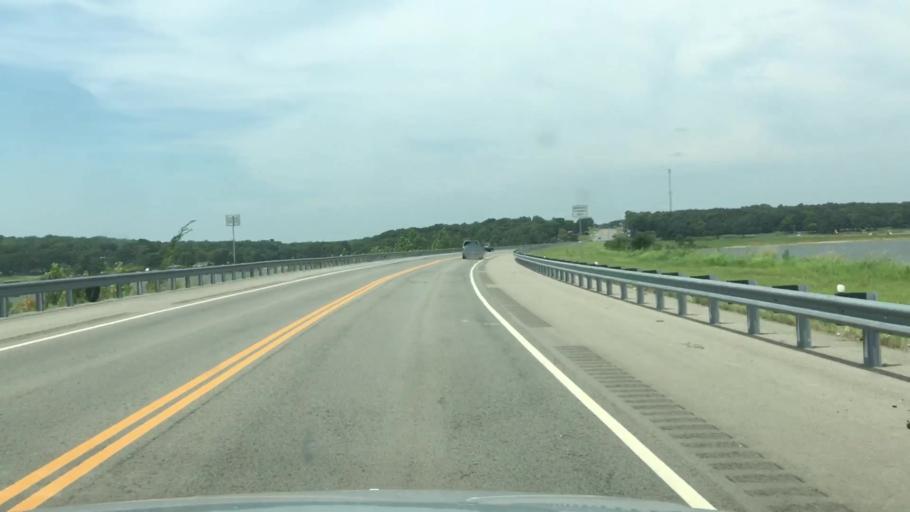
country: US
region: Oklahoma
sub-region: Wagoner County
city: Wagoner
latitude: 35.9316
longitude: -95.2735
